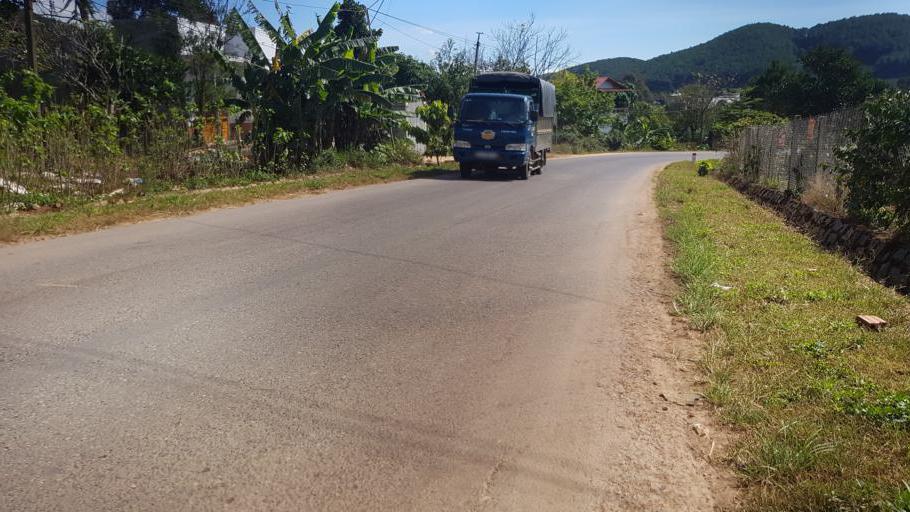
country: VN
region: Lam Dong
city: Da Lat
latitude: 11.8779
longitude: 108.3426
